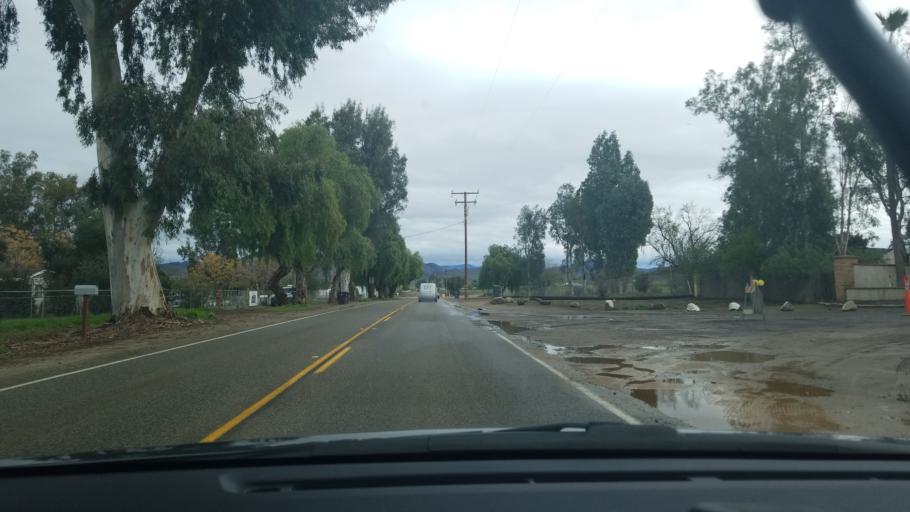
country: US
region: California
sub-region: Riverside County
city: Winchester
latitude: 33.6417
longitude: -117.1130
